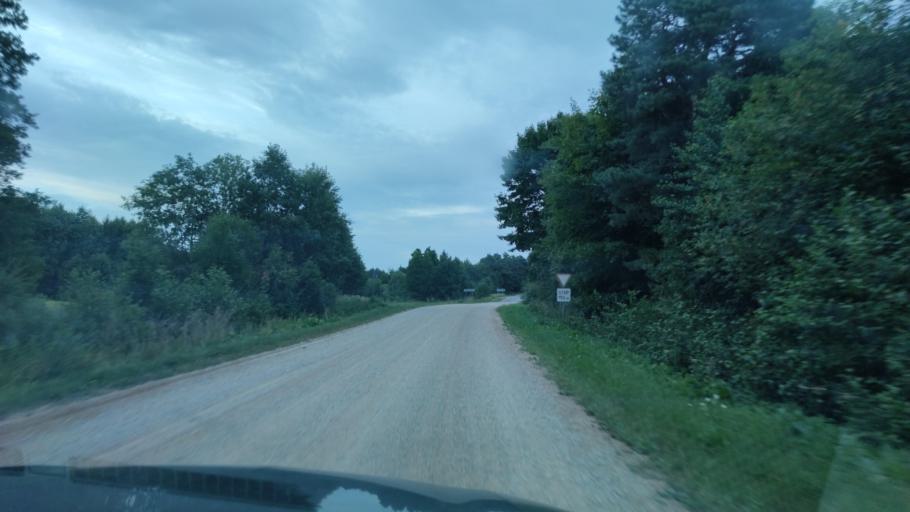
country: BY
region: Vitebsk
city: Mosar
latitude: 55.0743
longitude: 27.2147
